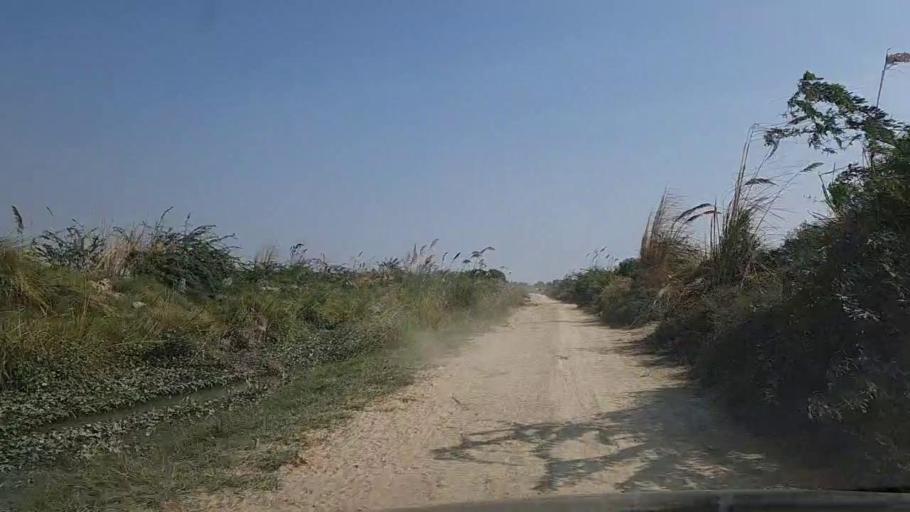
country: PK
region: Sindh
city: Gharo
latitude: 24.7134
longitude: 67.5868
